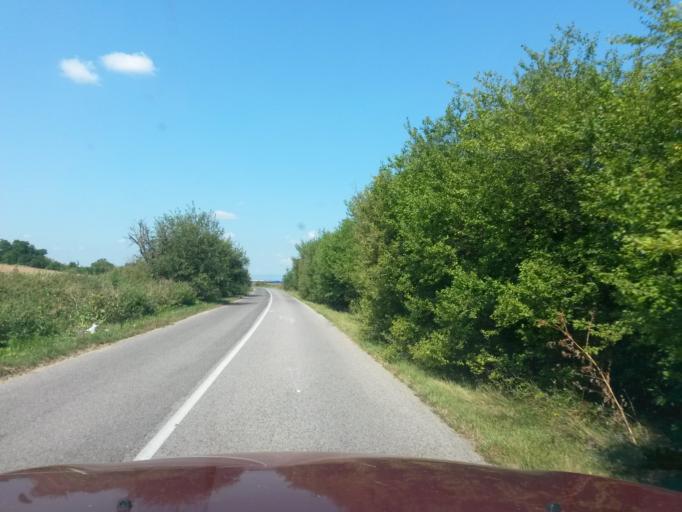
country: SK
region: Kosicky
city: Moldava nad Bodvou
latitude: 48.5324
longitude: 21.1005
